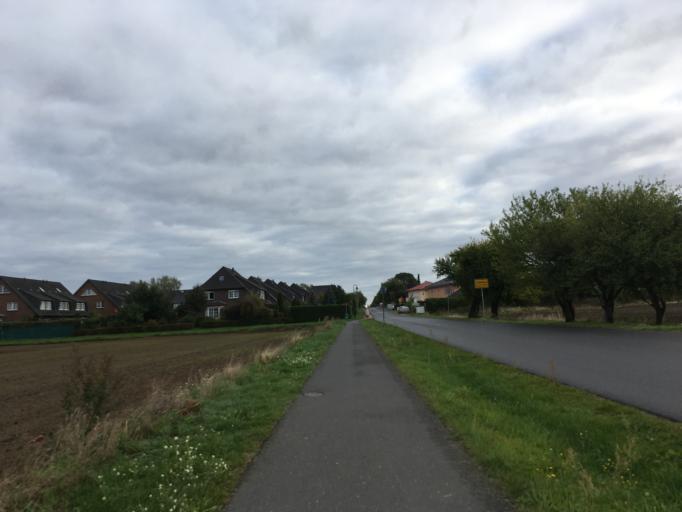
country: DE
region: Berlin
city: Falkenberg
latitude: 52.5970
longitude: 13.5523
